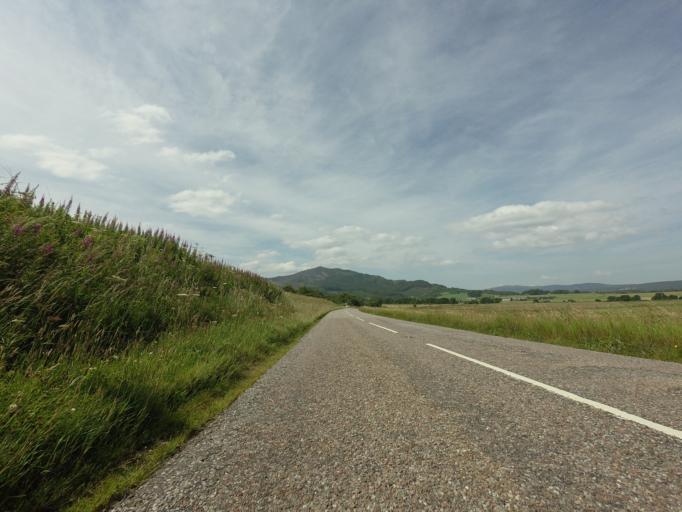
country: GB
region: Scotland
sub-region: Highland
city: Tain
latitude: 57.8399
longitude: -4.1912
